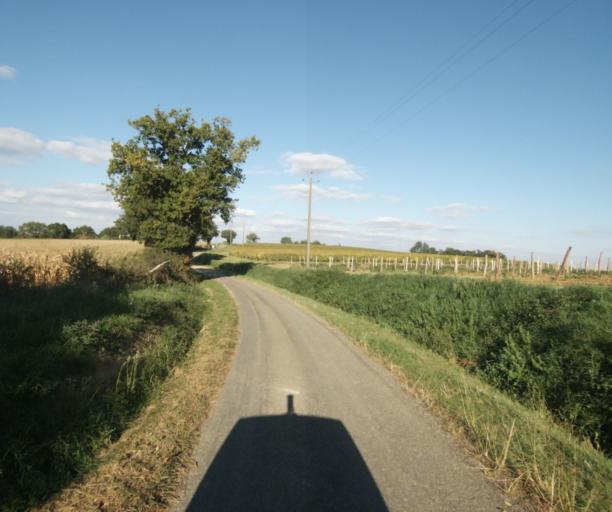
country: FR
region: Midi-Pyrenees
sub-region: Departement du Gers
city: Eauze
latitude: 43.7950
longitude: 0.1237
